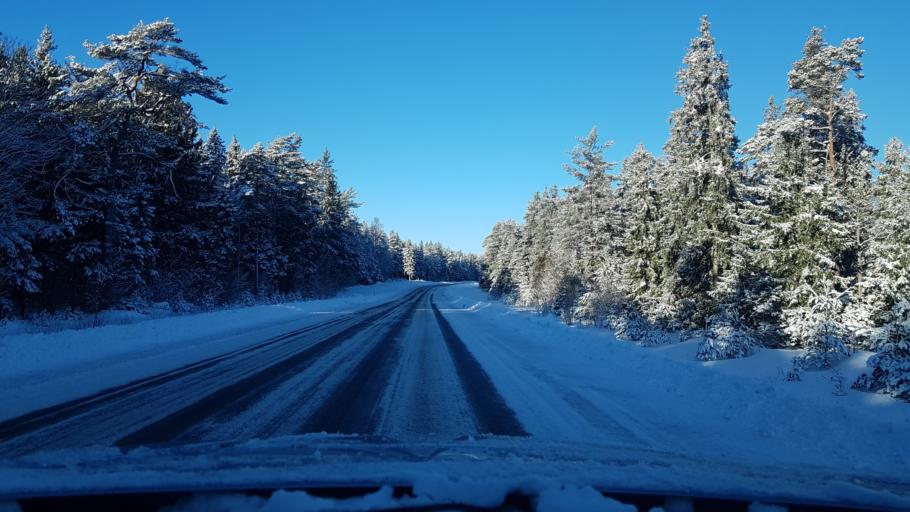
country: EE
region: Hiiumaa
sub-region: Kaerdla linn
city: Kardla
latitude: 58.9641
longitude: 22.8393
